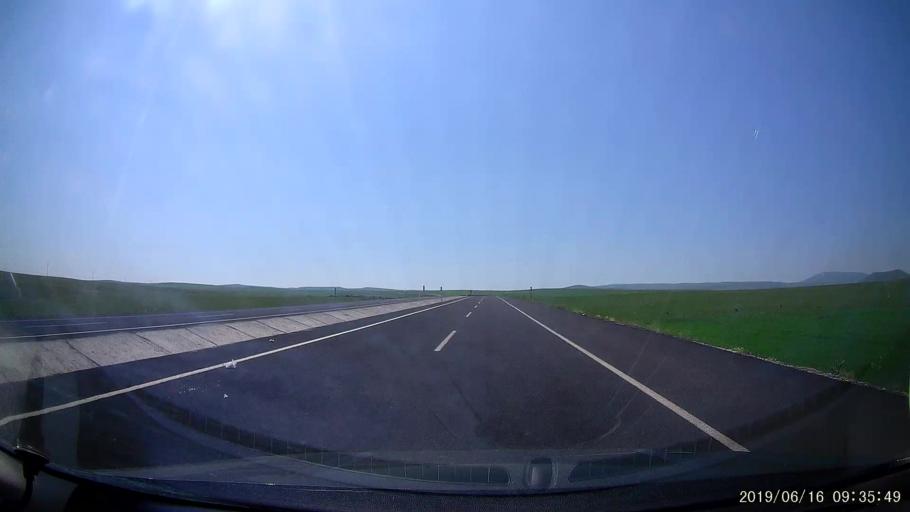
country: TR
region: Kars
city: Kars
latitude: 40.5658
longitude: 43.1622
